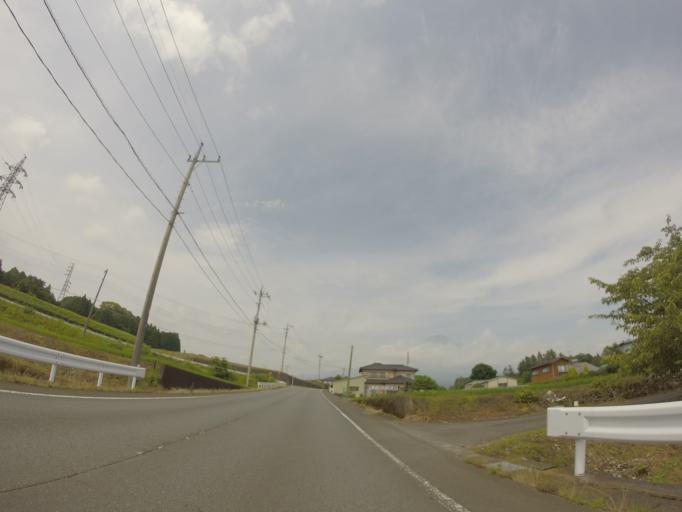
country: JP
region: Shizuoka
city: Fujinomiya
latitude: 35.2981
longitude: 138.5868
